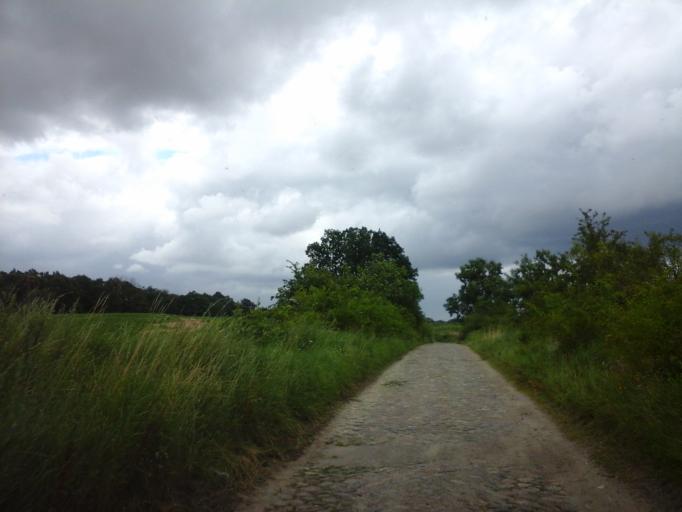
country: PL
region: West Pomeranian Voivodeship
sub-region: Powiat choszczenski
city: Pelczyce
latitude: 52.9953
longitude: 15.4009
